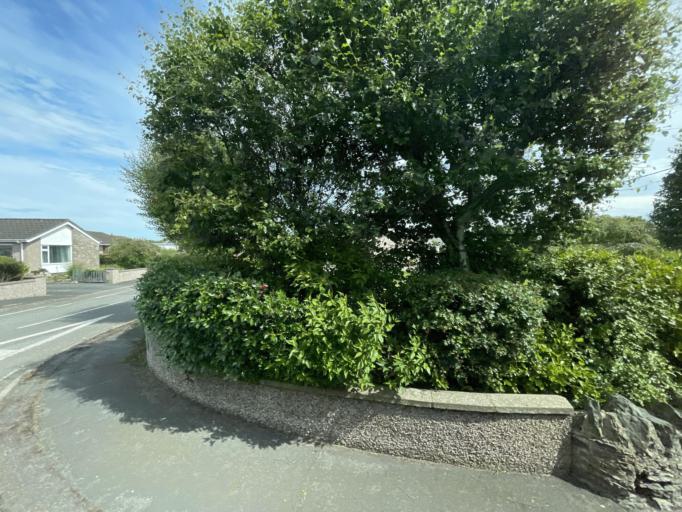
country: GB
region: Wales
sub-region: Anglesey
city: Valley
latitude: 53.2754
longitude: -4.5789
